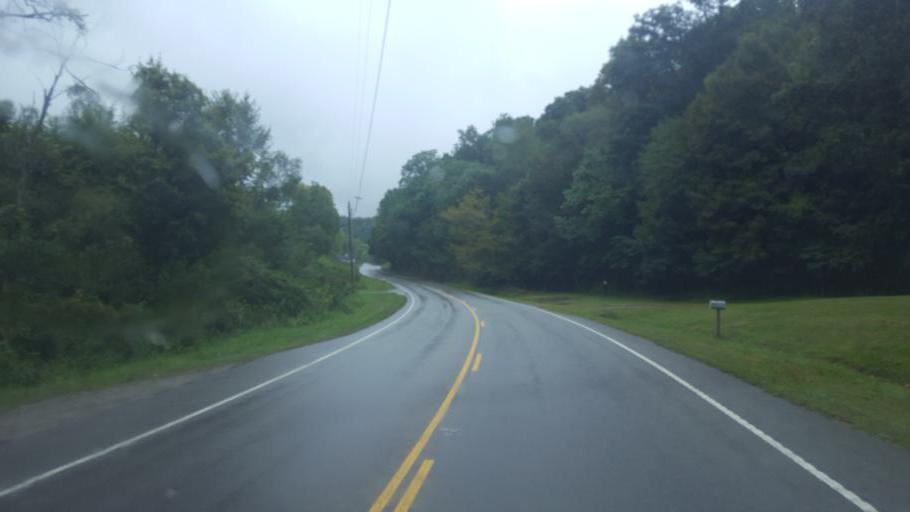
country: US
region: Ohio
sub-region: Jackson County
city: Oak Hill
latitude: 38.8333
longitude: -82.6541
